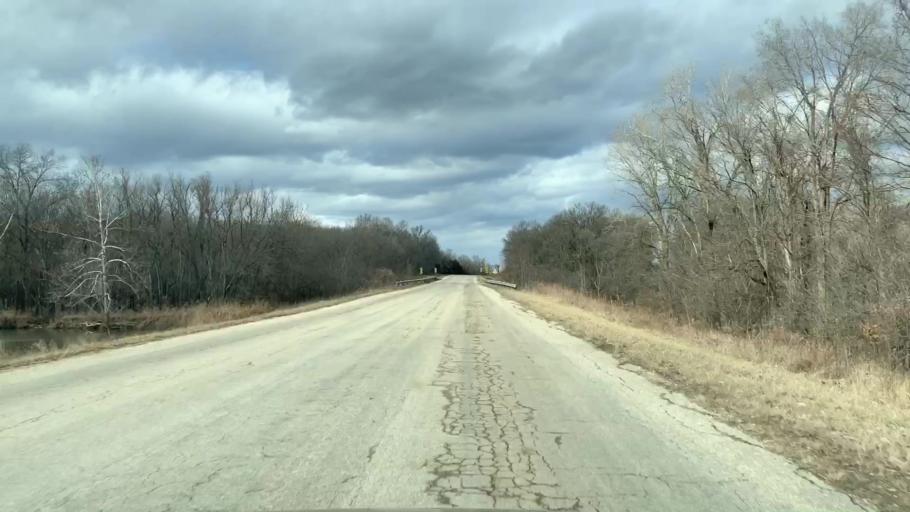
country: US
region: Kansas
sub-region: Allen County
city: Humboldt
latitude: 37.7521
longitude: -95.4708
